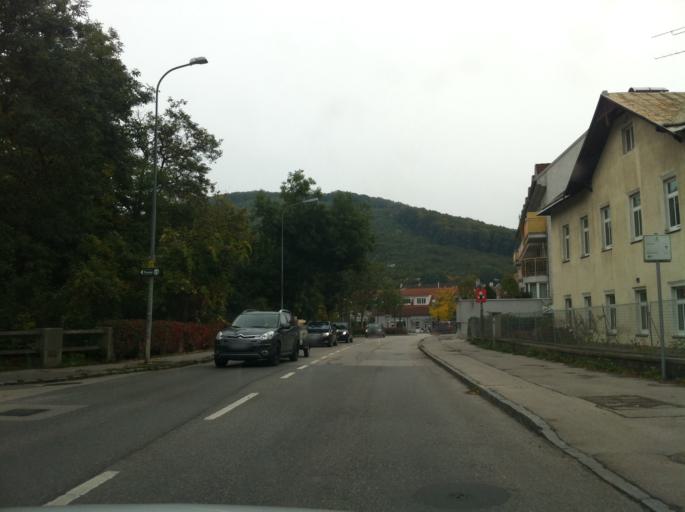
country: AT
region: Lower Austria
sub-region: Politischer Bezirk Wien-Umgebung
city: Purkersdorf
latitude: 48.2118
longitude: 16.1730
